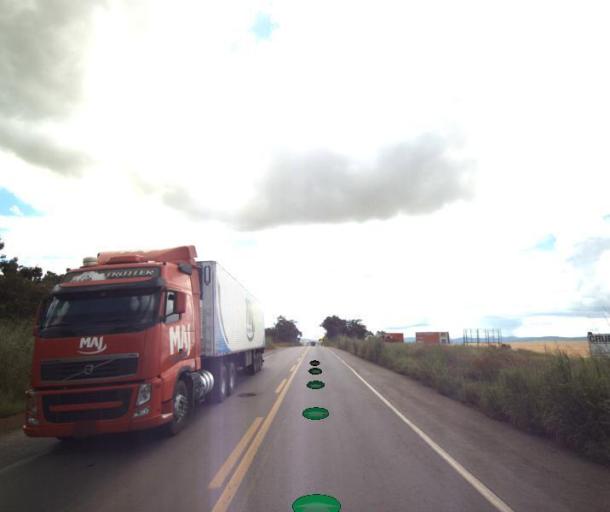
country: BR
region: Goias
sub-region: Jaragua
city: Jaragua
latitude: -15.8852
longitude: -49.2431
